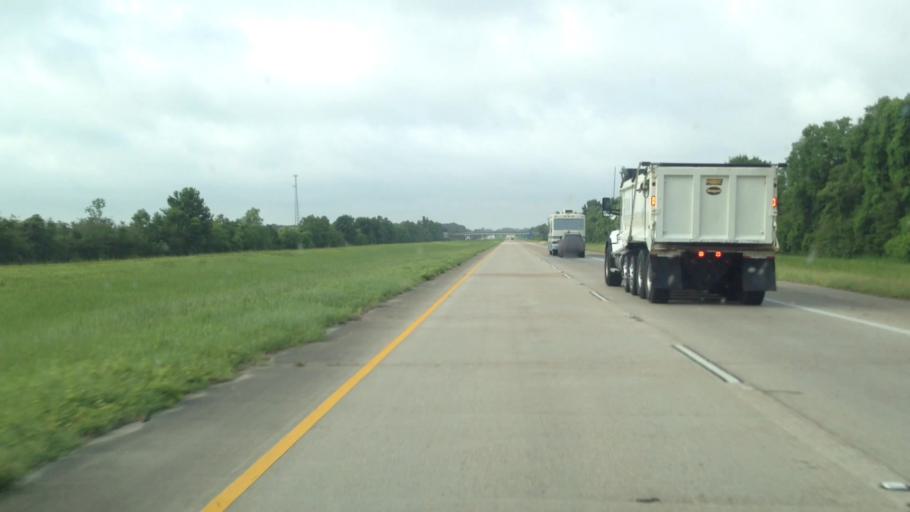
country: US
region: Louisiana
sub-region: Saint Landry Parish
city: Opelousas
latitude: 30.6294
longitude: -92.0479
